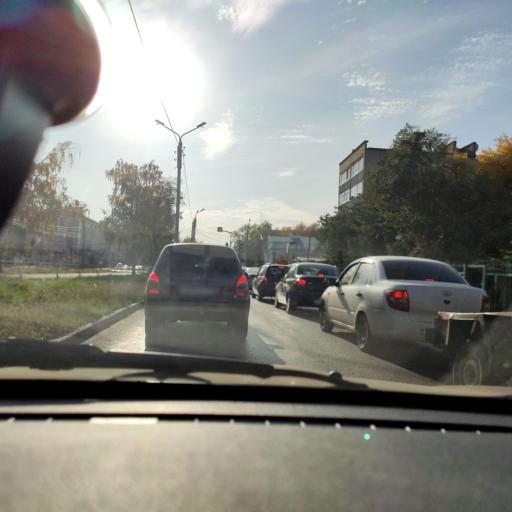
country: RU
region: Samara
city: Tol'yatti
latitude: 53.5193
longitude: 49.4030
